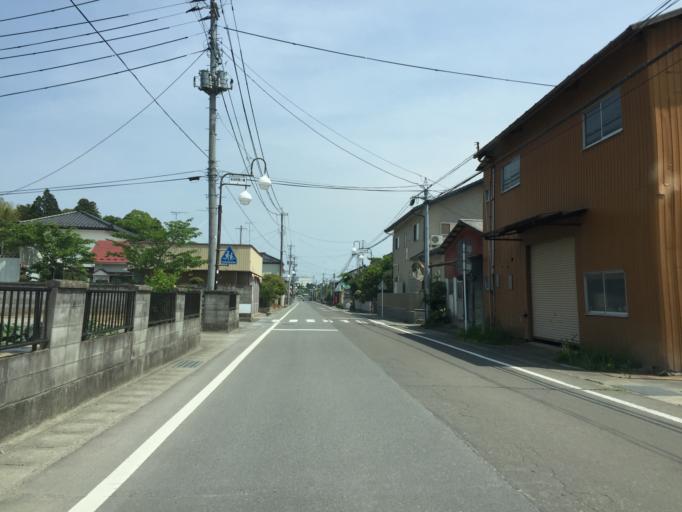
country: JP
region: Miyagi
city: Marumori
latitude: 37.8482
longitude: 140.9162
